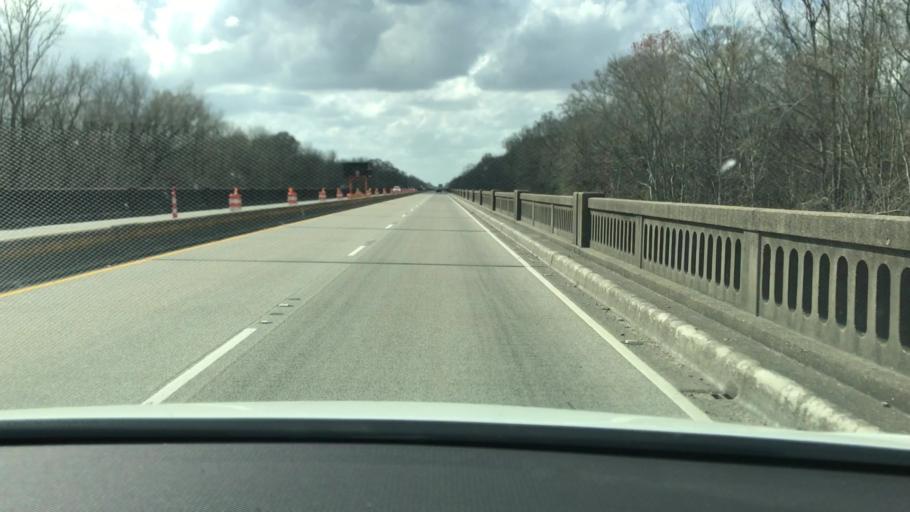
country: US
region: Louisiana
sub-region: Saint Landry Parish
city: Krotz Springs
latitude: 30.5559
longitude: -91.6710
